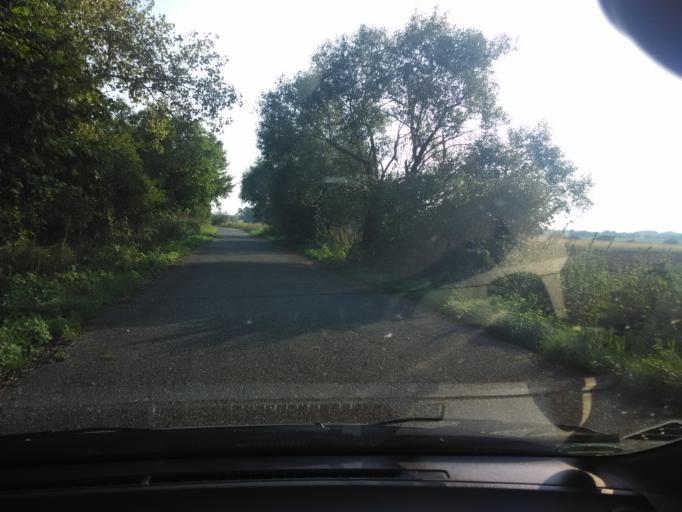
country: SK
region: Banskobystricky
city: Nova Bana
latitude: 48.3124
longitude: 18.7019
